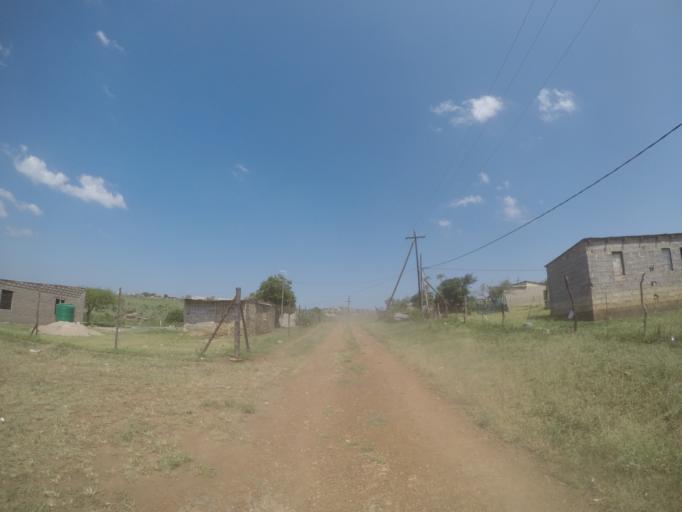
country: ZA
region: KwaZulu-Natal
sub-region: uThungulu District Municipality
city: Empangeni
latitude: -28.5891
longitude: 31.7431
